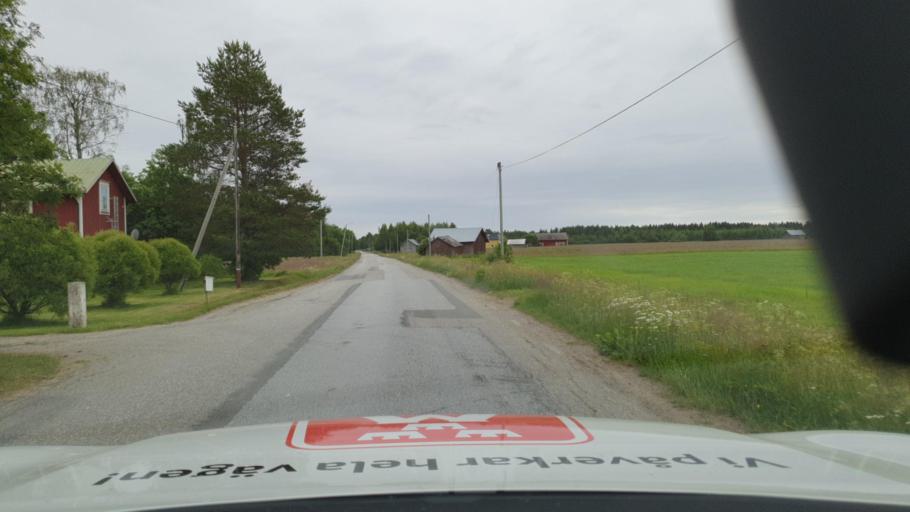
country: SE
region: Vaesterbotten
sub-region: Nordmalings Kommun
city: Nordmaling
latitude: 63.5419
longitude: 19.3943
